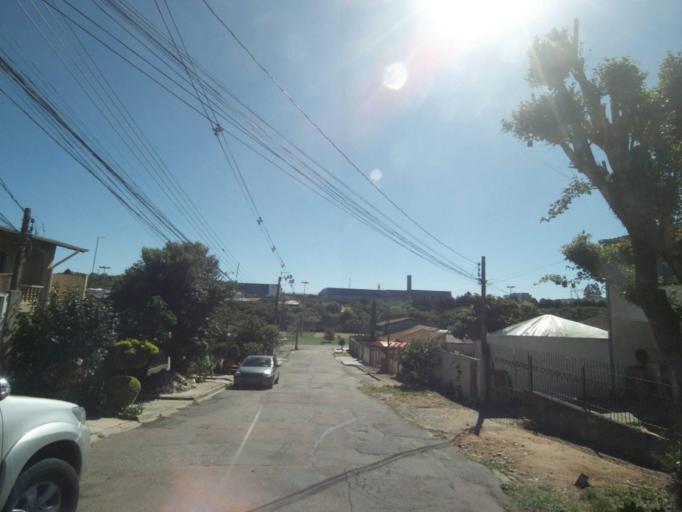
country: BR
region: Parana
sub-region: Curitiba
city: Curitiba
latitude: -25.4540
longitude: -49.3556
